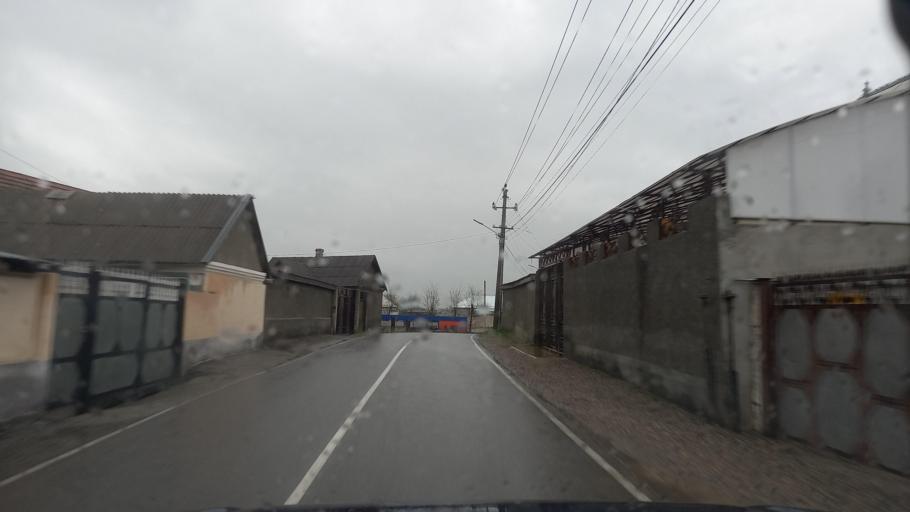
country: RU
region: Kabardino-Balkariya
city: Gundelen
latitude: 43.5952
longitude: 43.1737
